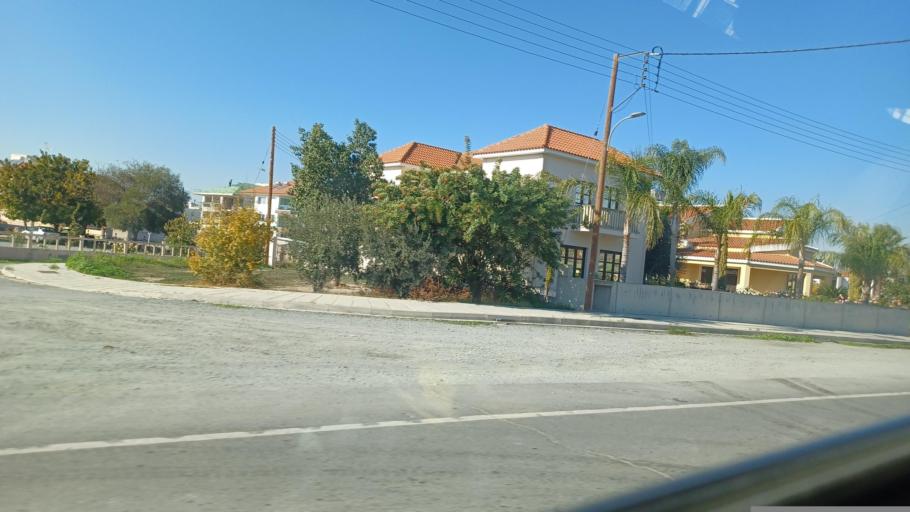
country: CY
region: Lefkosia
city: Alampra
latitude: 35.0060
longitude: 33.3939
